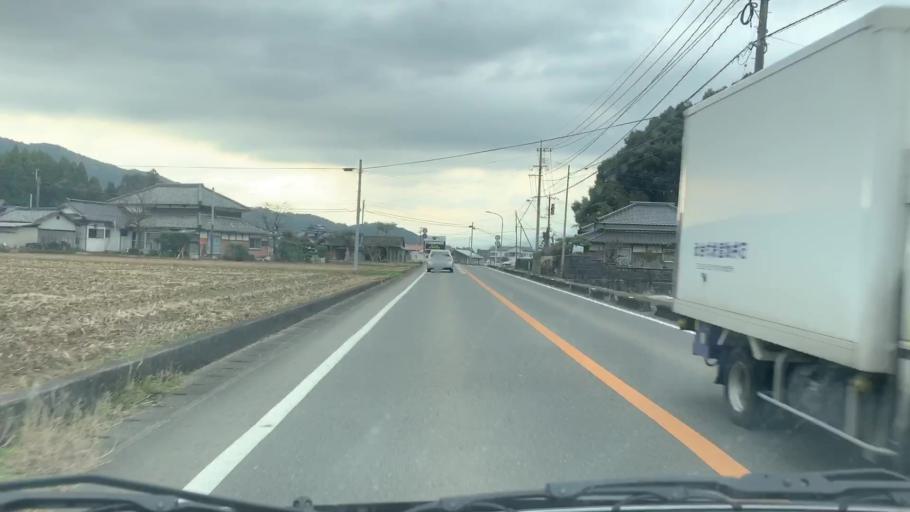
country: JP
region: Saga Prefecture
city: Kashima
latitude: 33.1529
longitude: 130.0645
